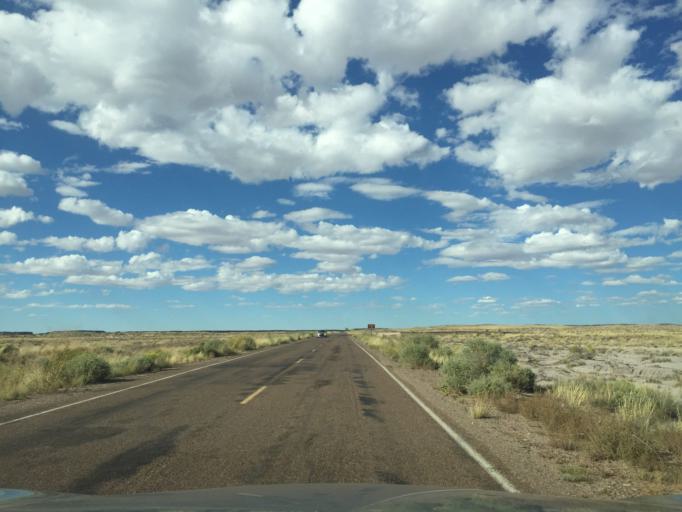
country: US
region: Arizona
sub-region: Navajo County
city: Holbrook
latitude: 34.9198
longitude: -109.7848
